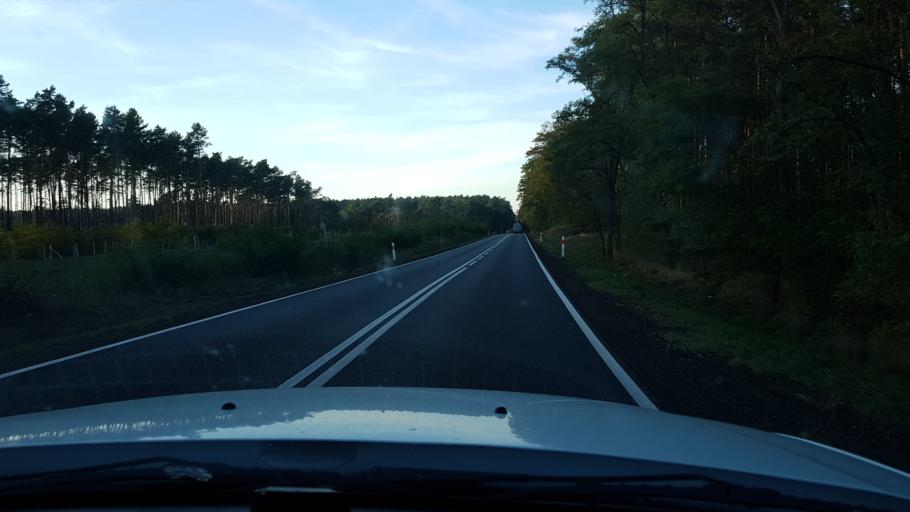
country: PL
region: West Pomeranian Voivodeship
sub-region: Powiat gryfinski
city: Chojna
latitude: 52.9712
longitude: 14.3819
